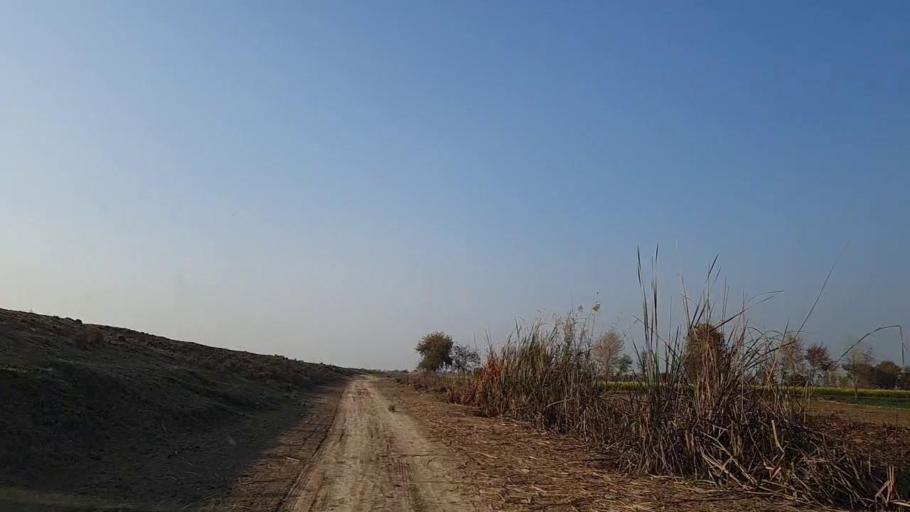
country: PK
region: Sindh
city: Sakrand
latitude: 26.1008
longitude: 68.3672
